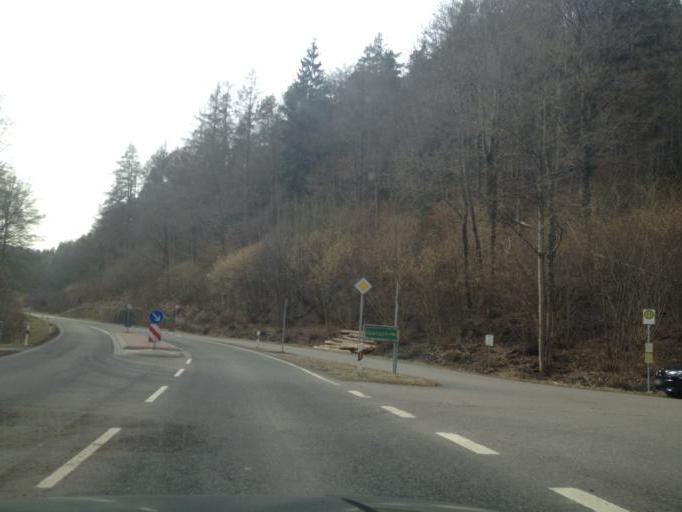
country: DE
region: Rheinland-Pfalz
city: Carlsberg
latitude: 49.4535
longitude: 8.0369
